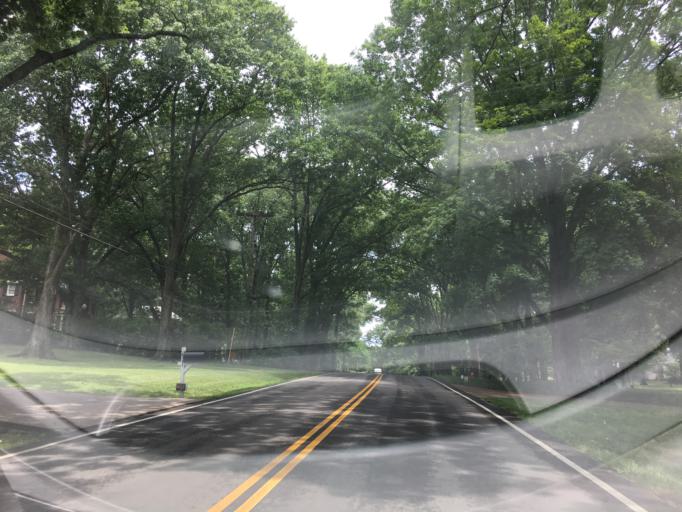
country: US
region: Tennessee
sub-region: Davidson County
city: Belle Meade
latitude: 36.0981
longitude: -86.8466
